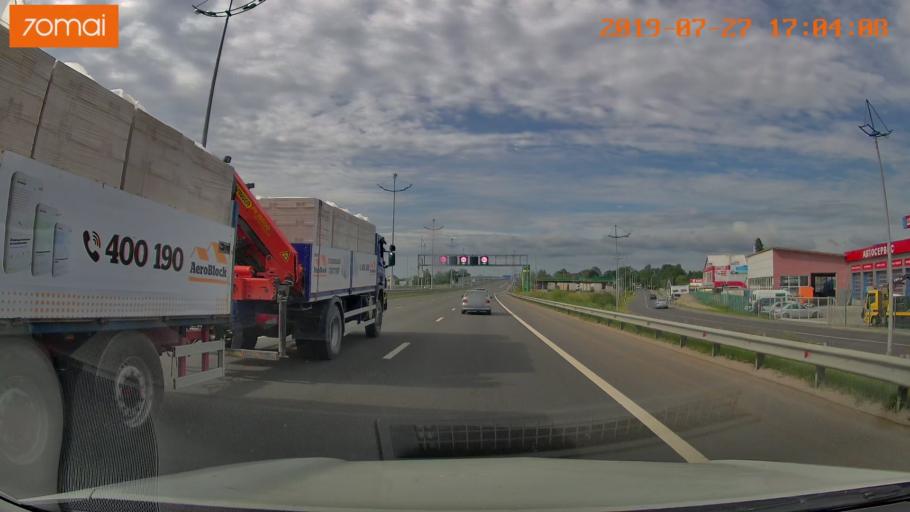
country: RU
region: Kaliningrad
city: Bol'shoe Isakovo
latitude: 54.7110
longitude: 20.5974
